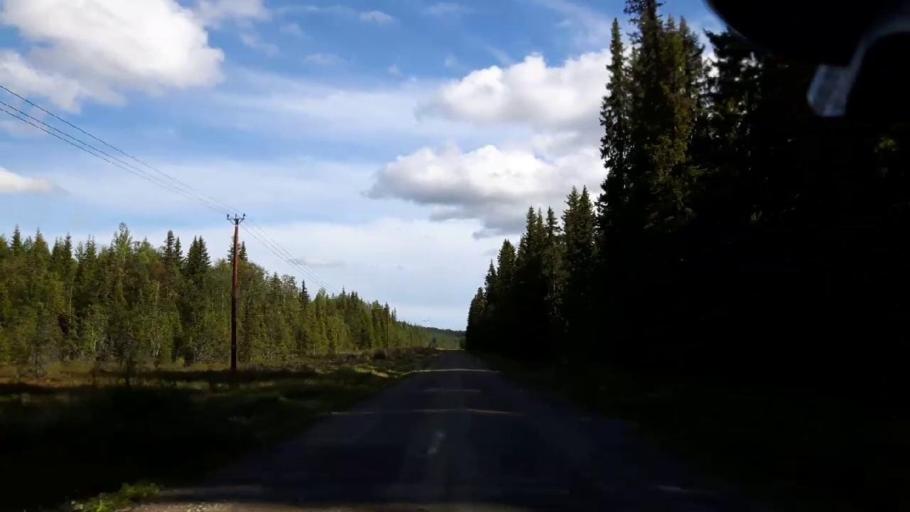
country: SE
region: Jaemtland
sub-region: Ragunda Kommun
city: Hammarstrand
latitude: 63.4327
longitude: 16.0399
